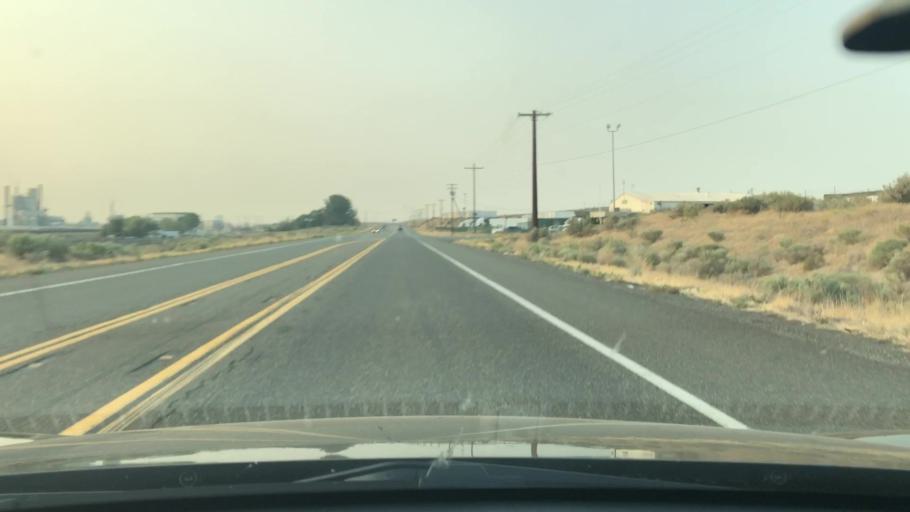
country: US
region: Washington
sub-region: Benton County
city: Finley
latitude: 46.0945
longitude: -118.9116
